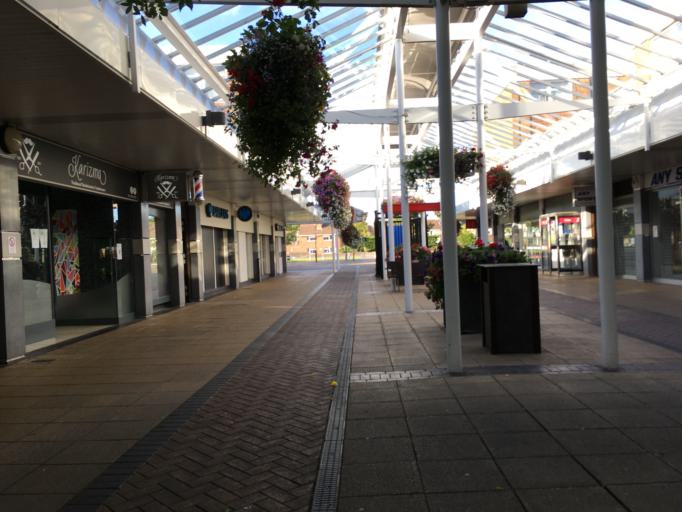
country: GB
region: England
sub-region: South Gloucestershire
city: Yate
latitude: 51.5409
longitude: -2.4132
